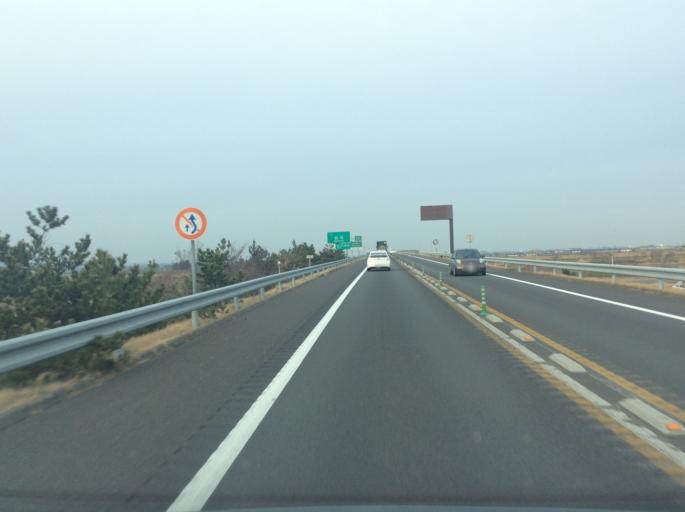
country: JP
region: Miyagi
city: Iwanuma
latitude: 38.0913
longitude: 140.8872
